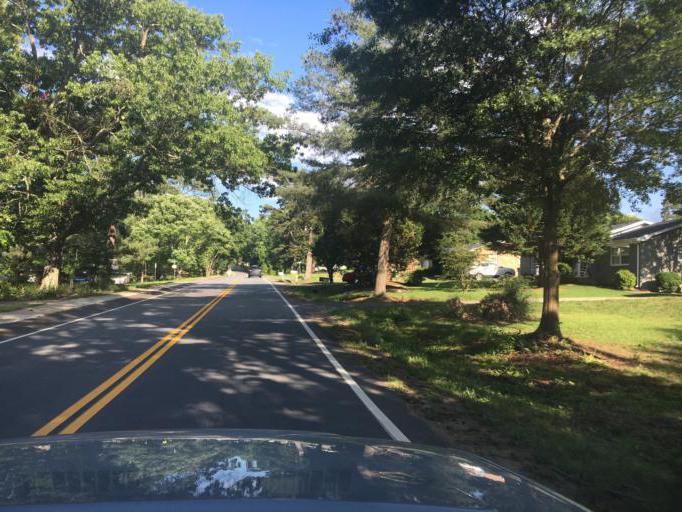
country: US
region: South Carolina
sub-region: Greenville County
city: Mauldin
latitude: 34.7806
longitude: -82.2901
